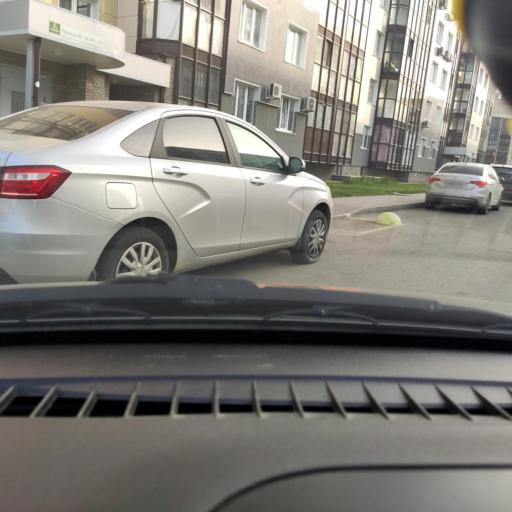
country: RU
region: Samara
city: Tol'yatti
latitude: 53.5298
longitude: 49.3419
